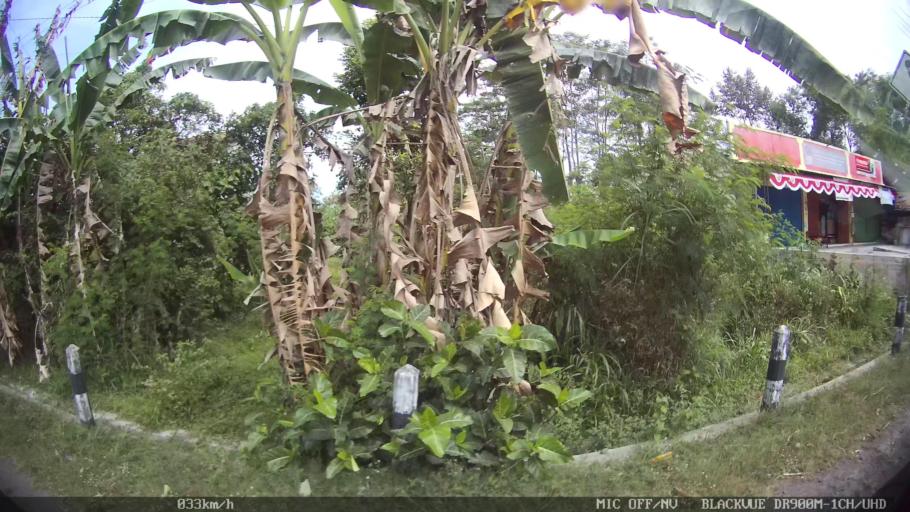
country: ID
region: Central Java
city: Candi Prambanan
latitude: -7.7348
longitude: 110.4729
